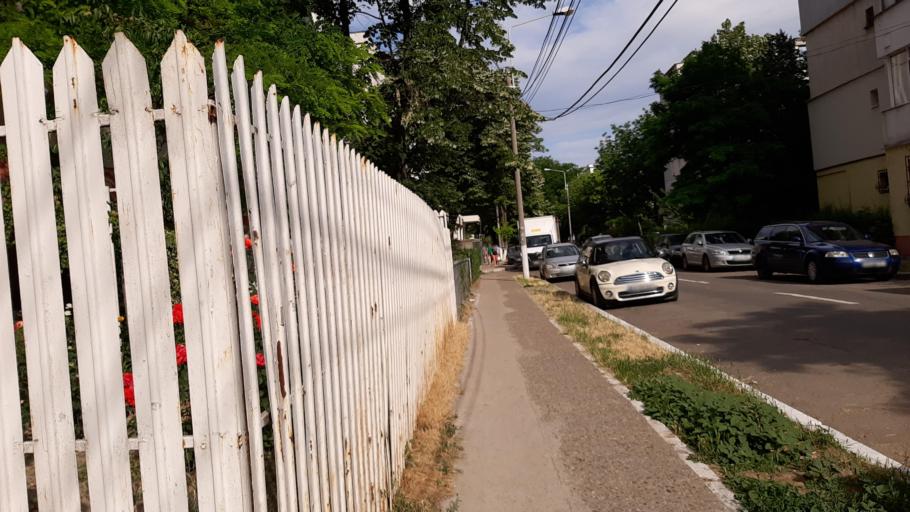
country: RO
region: Galati
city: Galati
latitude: 45.4442
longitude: 28.0237
